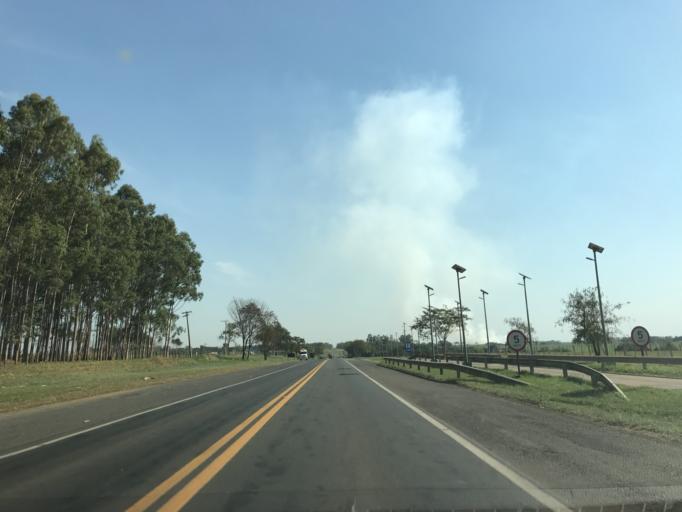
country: BR
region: Sao Paulo
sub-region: Penapolis
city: Penapolis
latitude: -21.3794
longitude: -50.0884
